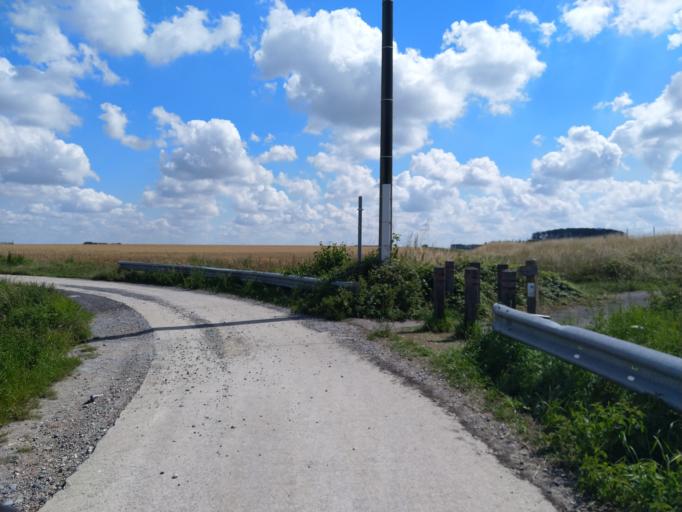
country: BE
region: Wallonia
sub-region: Province du Hainaut
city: Beloeil
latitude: 50.5699
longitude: 3.6891
